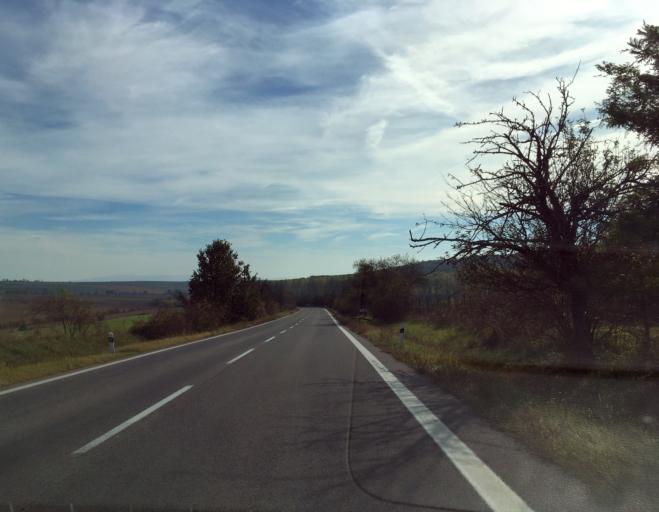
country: SK
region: Nitriansky
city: Svodin
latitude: 48.0347
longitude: 18.4416
